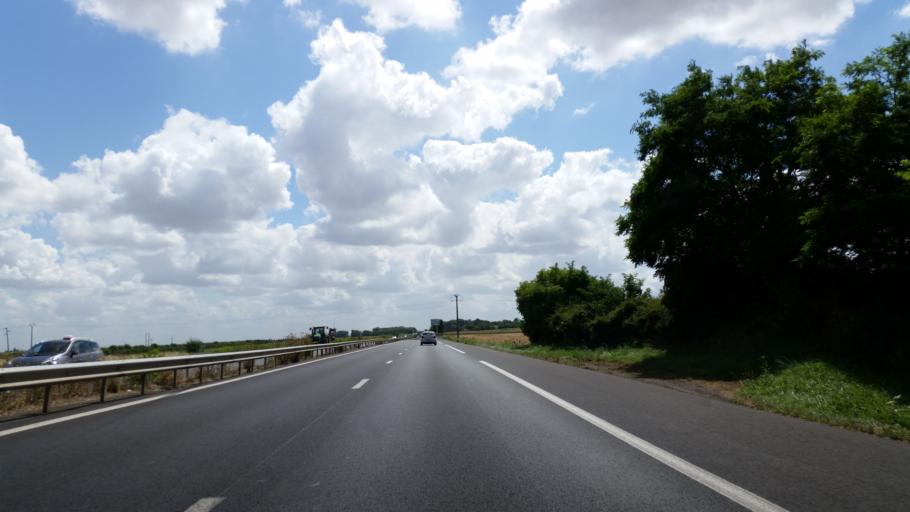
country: FR
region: Lower Normandy
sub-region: Departement du Calvados
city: Bretteville-sur-Laize
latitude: 49.0556
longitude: -0.2873
